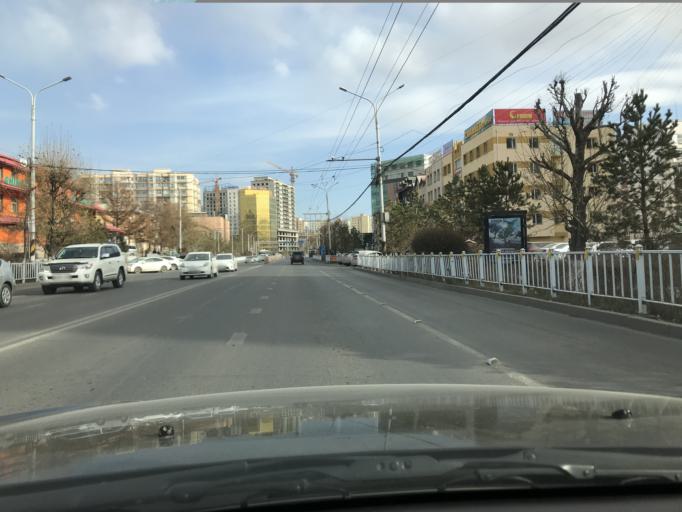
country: MN
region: Ulaanbaatar
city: Ulaanbaatar
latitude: 47.9187
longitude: 106.9385
